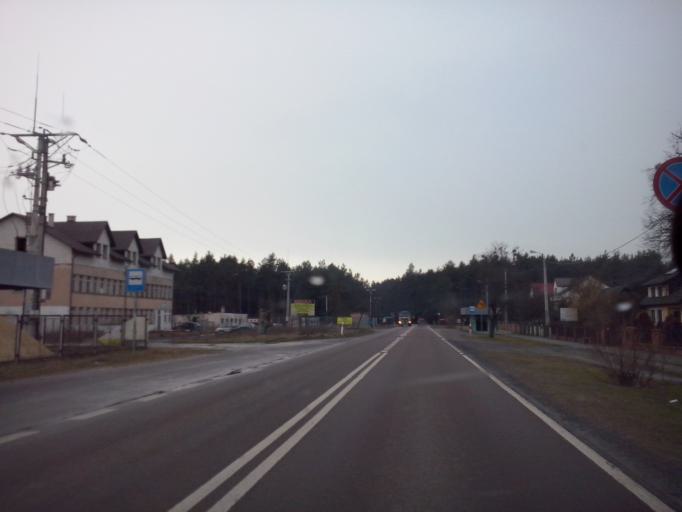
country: PL
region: Lublin Voivodeship
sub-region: Powiat bilgorajski
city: Tereszpol
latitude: 50.5820
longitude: 22.8017
